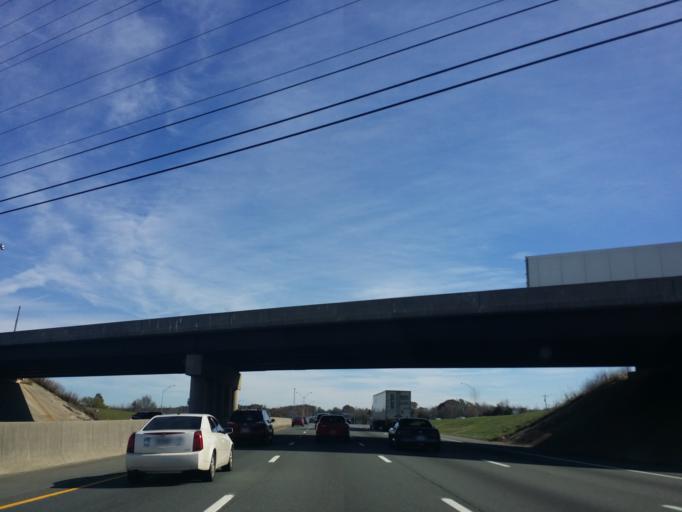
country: US
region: North Carolina
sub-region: Alamance County
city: Haw River
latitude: 36.0687
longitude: -79.3539
